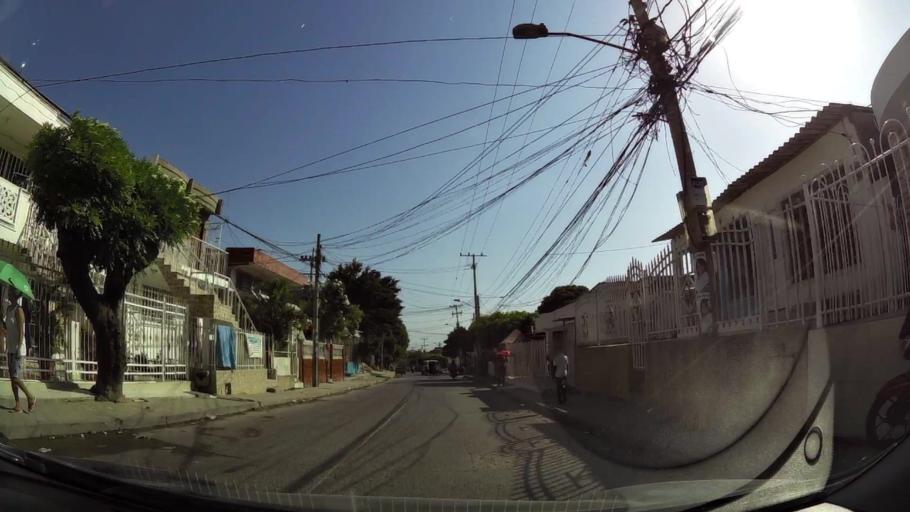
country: CO
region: Bolivar
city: Cartagena
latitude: 10.4258
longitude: -75.5201
